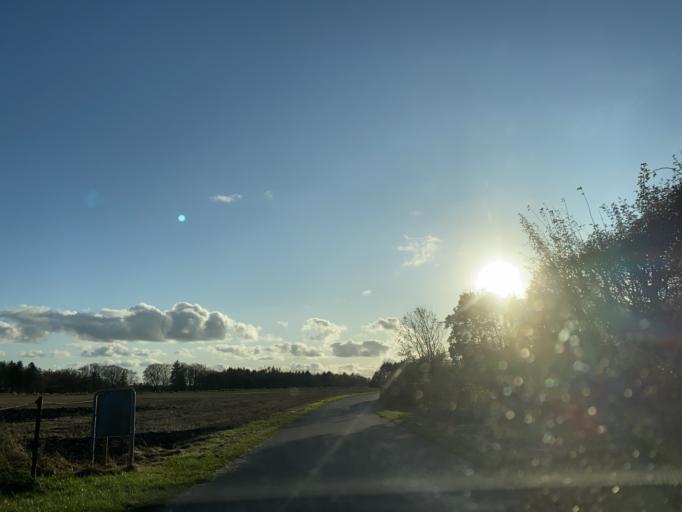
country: DK
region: Central Jutland
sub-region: Viborg Kommune
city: Bjerringbro
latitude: 56.3178
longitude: 9.6986
